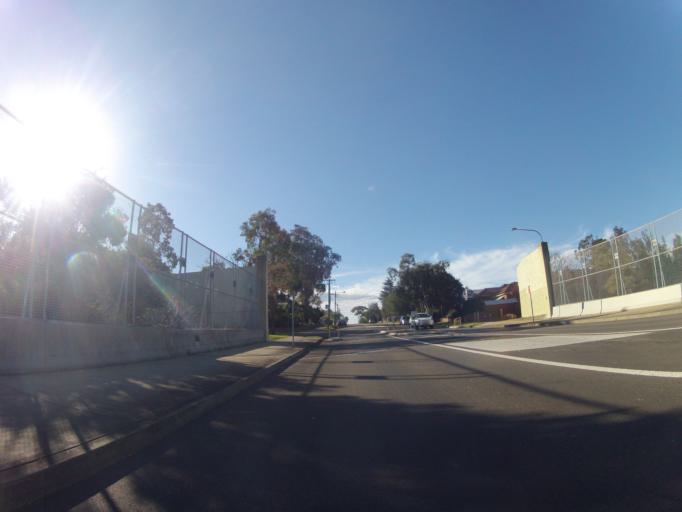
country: AU
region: New South Wales
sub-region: Canterbury
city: Roselands
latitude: -33.9422
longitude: 151.0801
